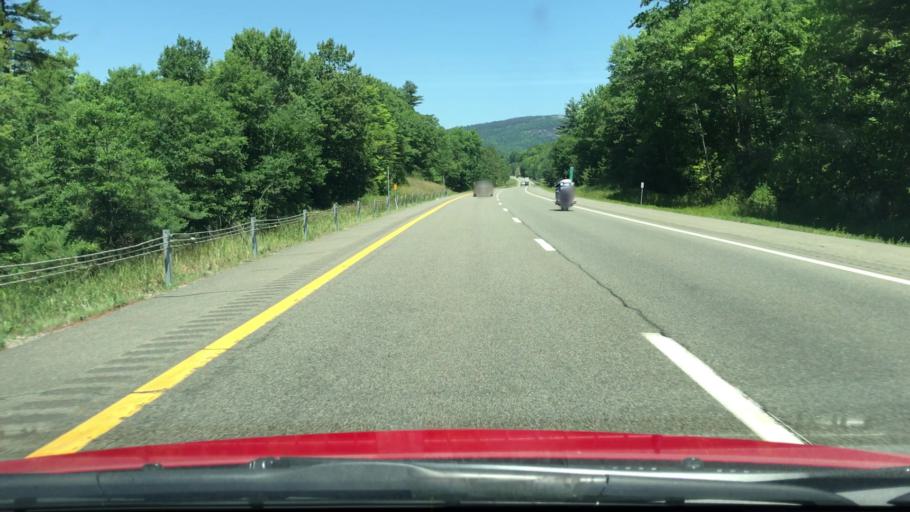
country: US
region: New York
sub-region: Essex County
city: Elizabethtown
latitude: 44.3537
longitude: -73.5328
